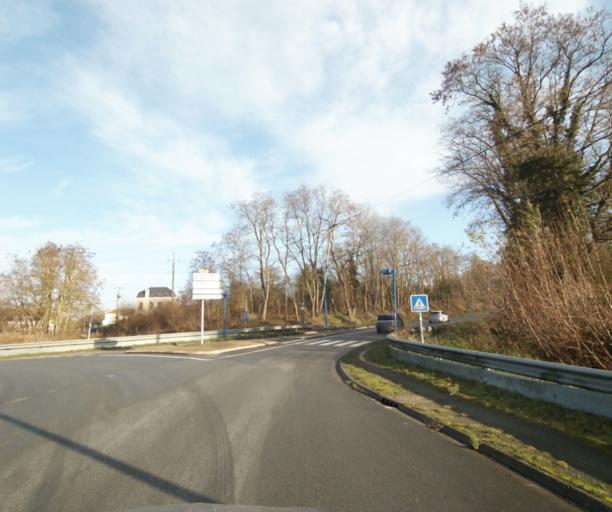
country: FR
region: Nord-Pas-de-Calais
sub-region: Departement du Nord
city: Trith-Saint-Leger
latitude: 50.3218
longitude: 3.4995
